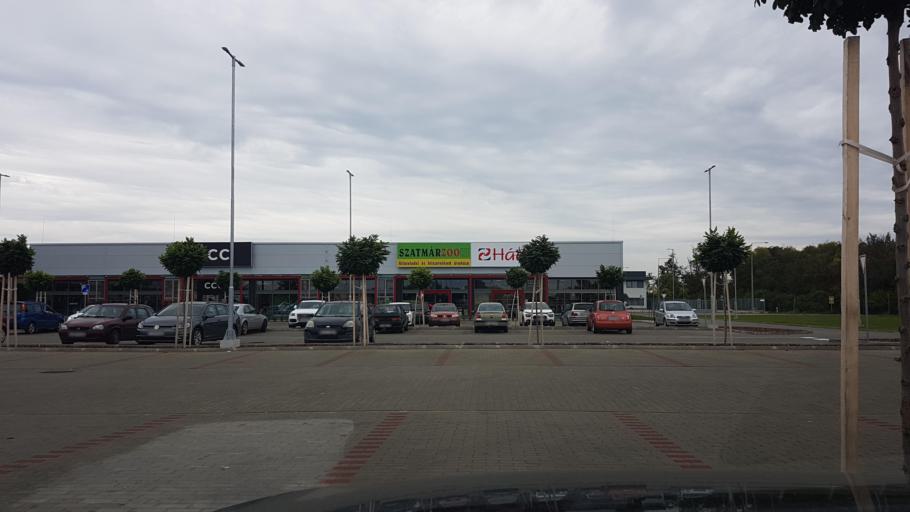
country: HU
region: Szabolcs-Szatmar-Bereg
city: Kisvarda
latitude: 48.2336
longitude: 22.0624
